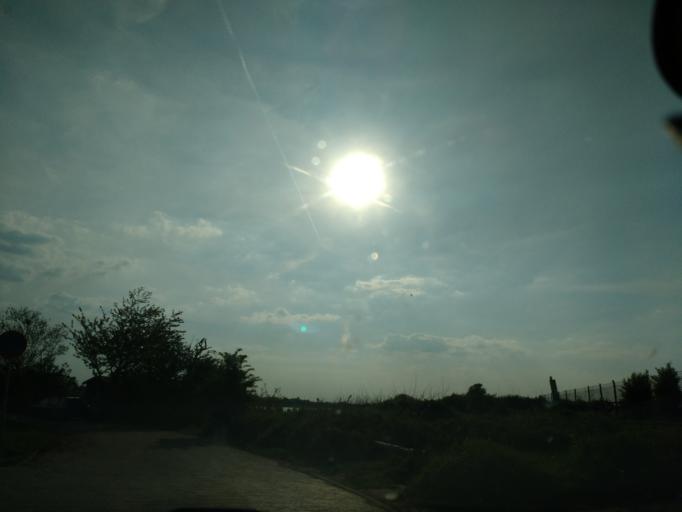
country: NL
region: Utrecht
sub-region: Gemeente Rhenen
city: Rhenen
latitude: 51.9429
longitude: 5.6160
